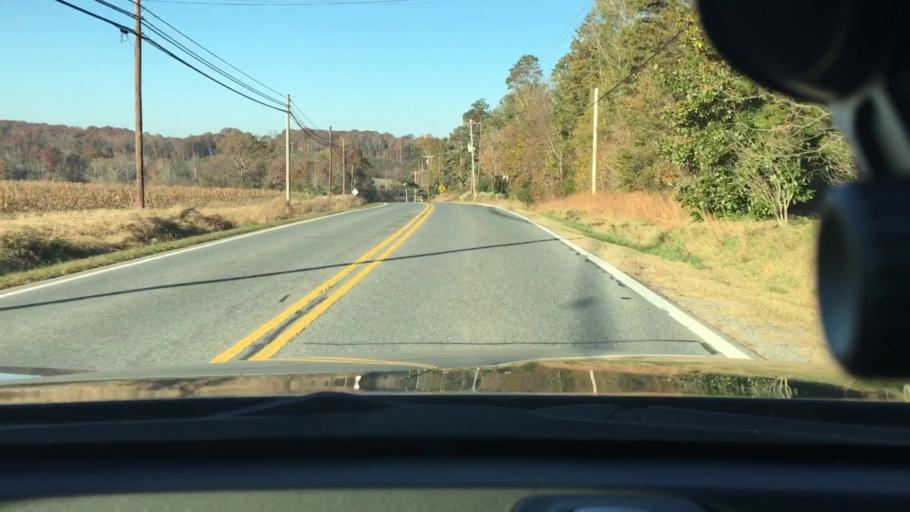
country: US
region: North Carolina
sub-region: Stanly County
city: Albemarle
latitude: 35.3587
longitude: -80.2305
